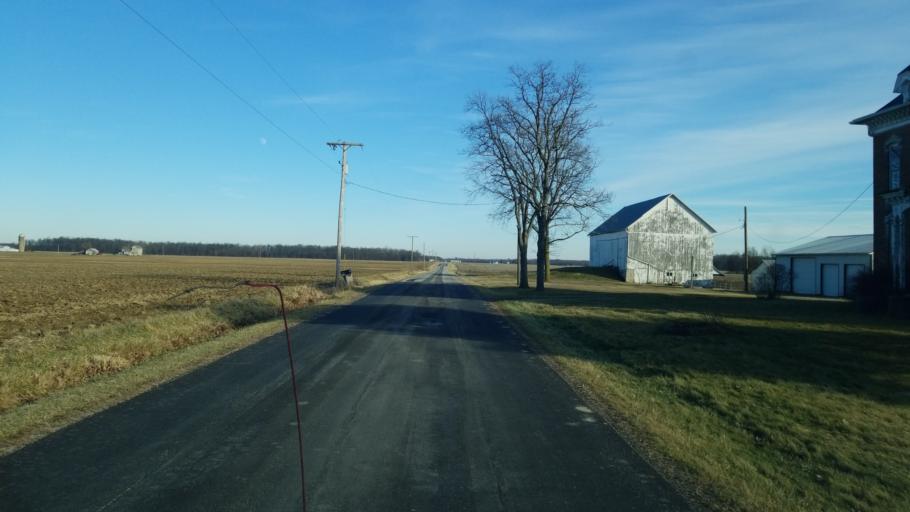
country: US
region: Ohio
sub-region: Huron County
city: Bellevue
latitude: 41.1800
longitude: -82.8148
